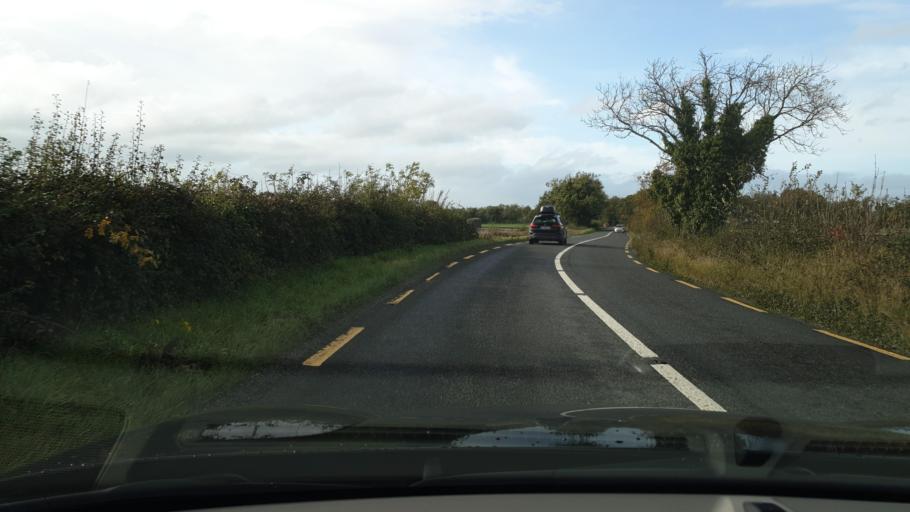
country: IE
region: Leinster
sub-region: An Mhi
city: Dunshaughlin
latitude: 53.5207
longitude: -6.5070
